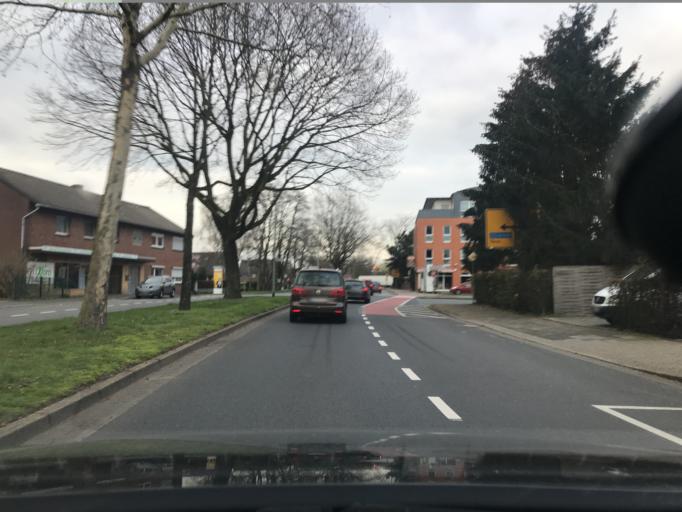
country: DE
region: North Rhine-Westphalia
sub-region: Regierungsbezirk Dusseldorf
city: Wesel
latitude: 51.6699
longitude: 6.6352
